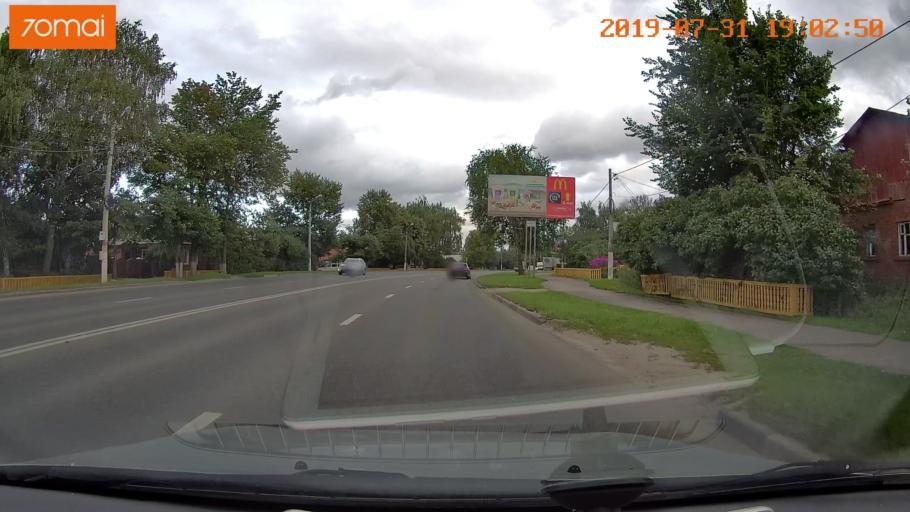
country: RU
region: Moskovskaya
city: Raduzhnyy
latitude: 55.1185
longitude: 38.7348
